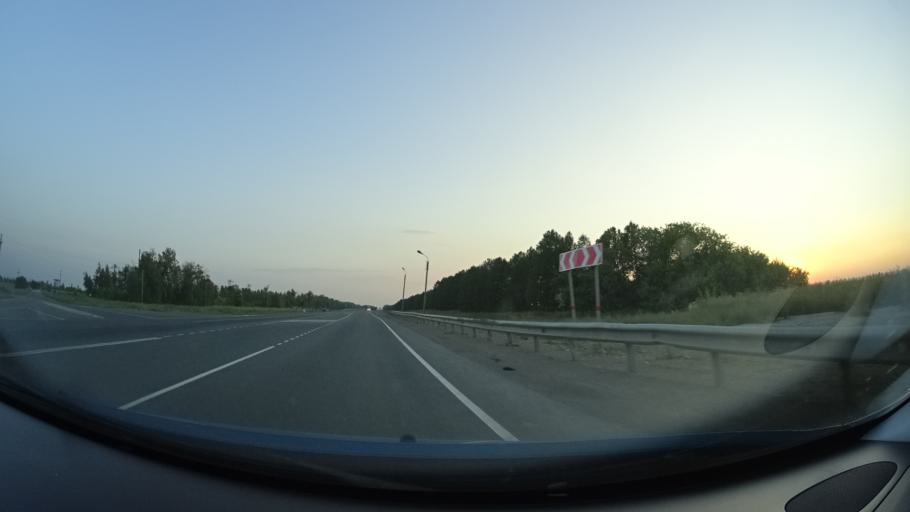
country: RU
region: Samara
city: Sukhodol
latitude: 53.8556
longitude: 51.1594
